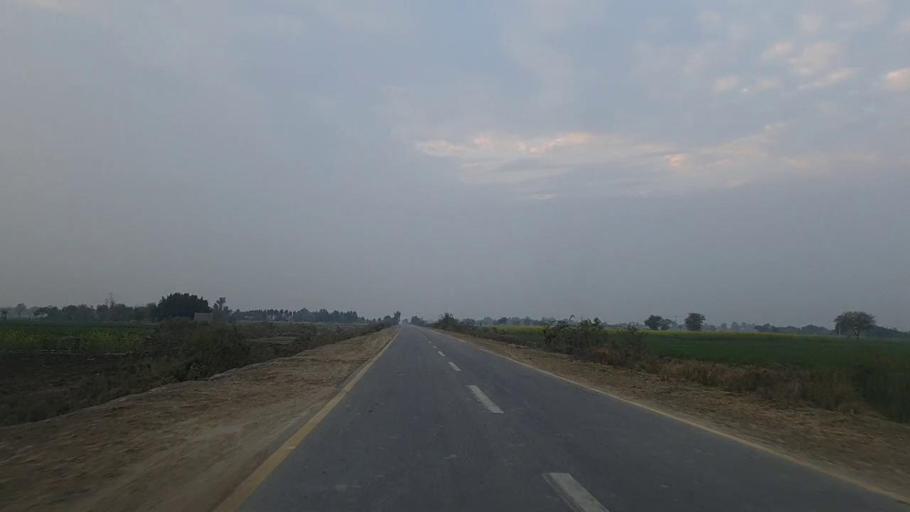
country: PK
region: Sindh
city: Jam Sahib
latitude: 26.3122
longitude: 68.5831
